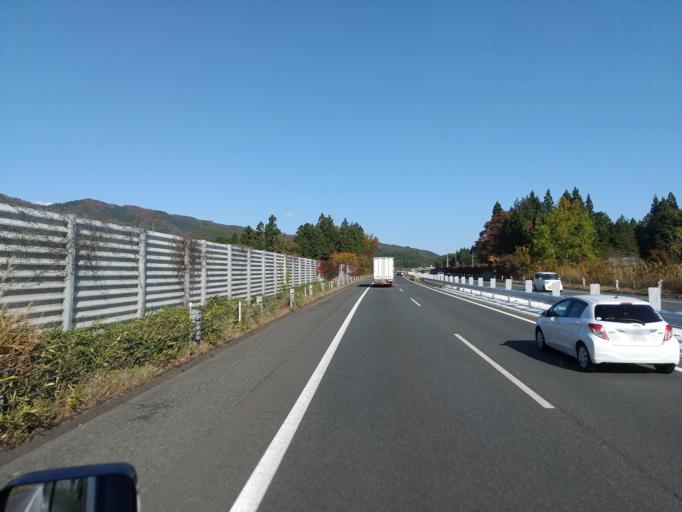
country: JP
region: Iwate
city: Hanamaki
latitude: 39.5034
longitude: 141.1023
